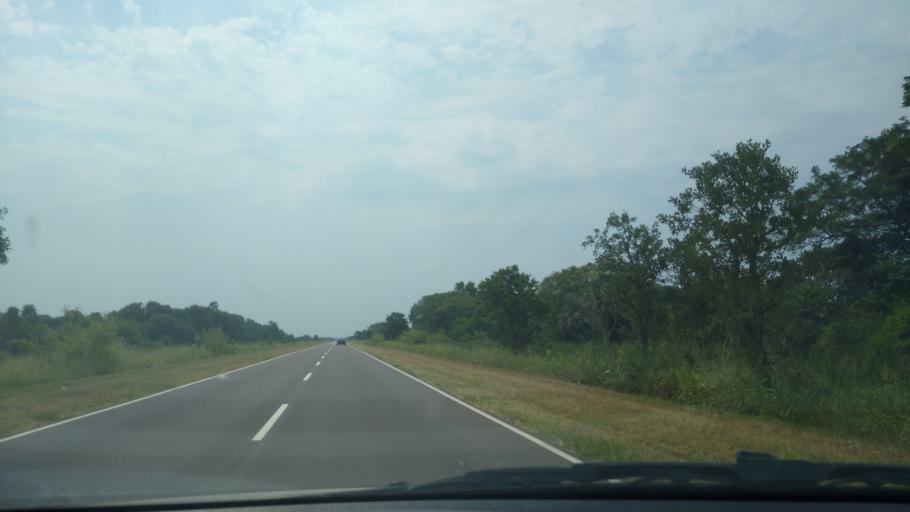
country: AR
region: Chaco
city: La Eduvigis
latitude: -27.0074
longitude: -58.9710
